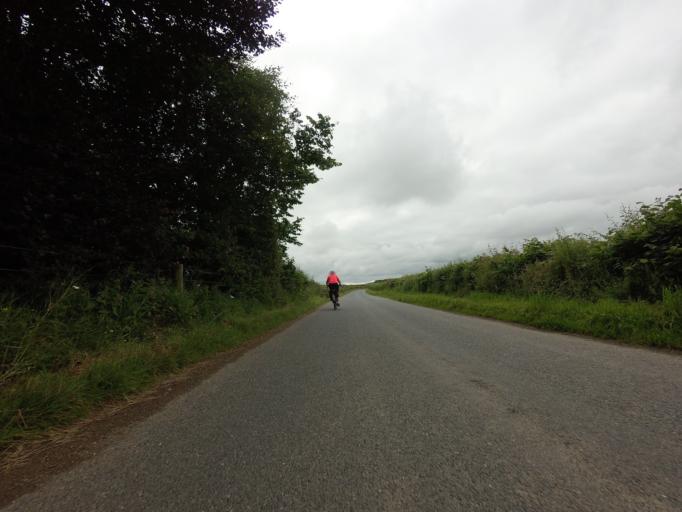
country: GB
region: Scotland
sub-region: Aberdeenshire
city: Rosehearty
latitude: 57.5368
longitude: -2.1847
